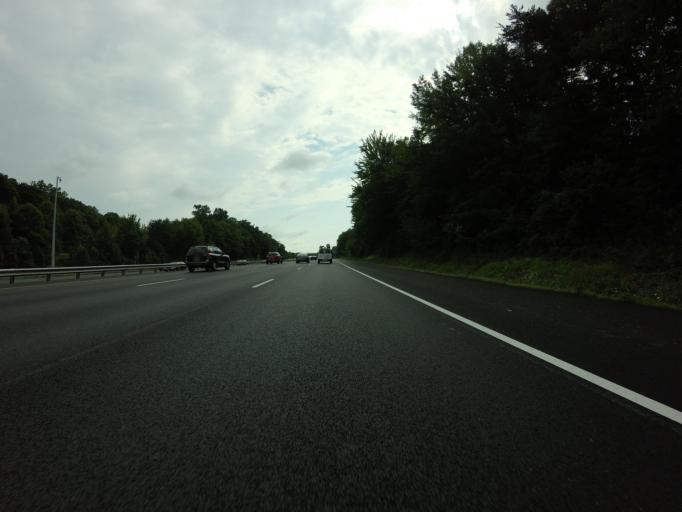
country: US
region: Maryland
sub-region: Harford County
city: Riverside
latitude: 39.4828
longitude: -76.2558
